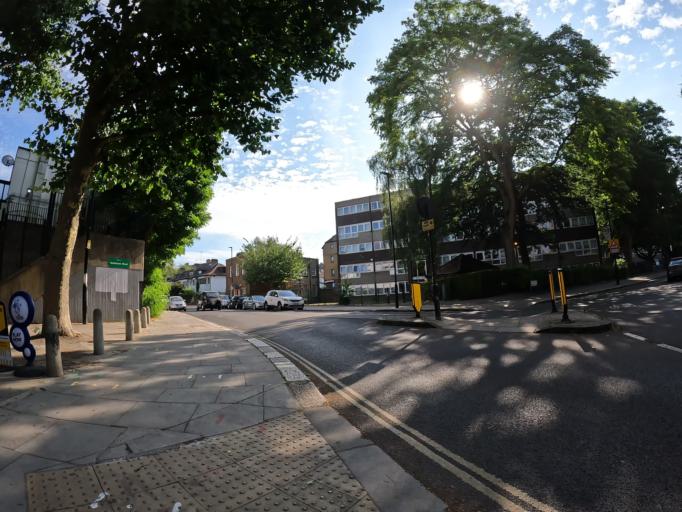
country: GB
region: England
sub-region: Greater London
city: Belsize Park
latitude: 51.5577
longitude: -0.1642
